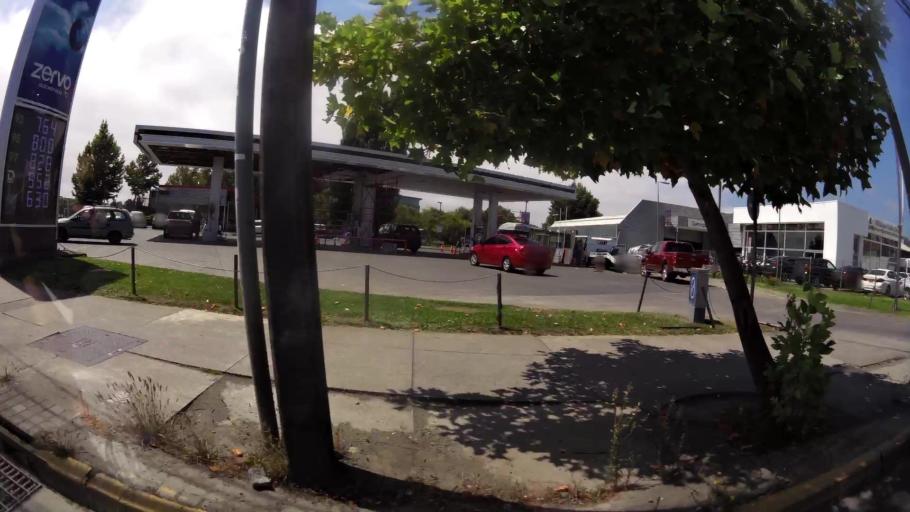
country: CL
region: Biobio
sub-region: Provincia de Concepcion
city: Concepcion
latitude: -36.8155
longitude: -73.0469
